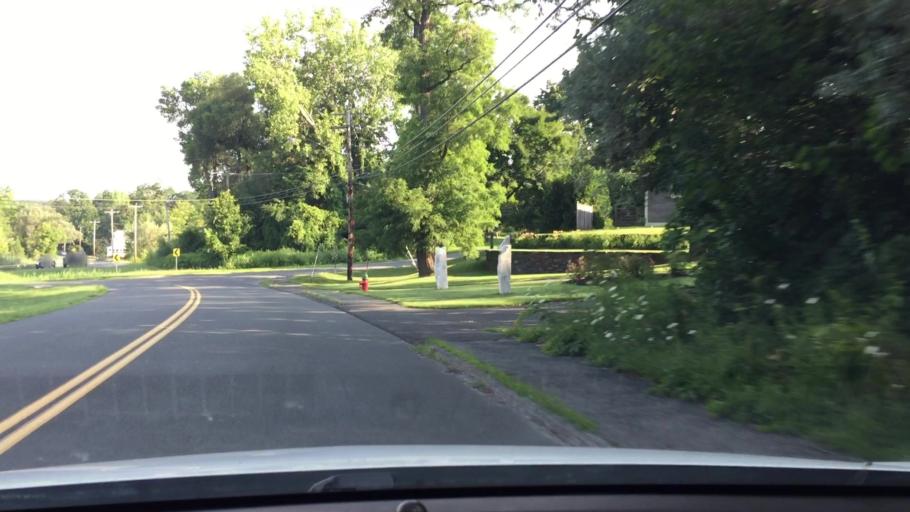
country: US
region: Massachusetts
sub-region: Berkshire County
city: Lee
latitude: 42.3252
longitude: -73.2392
